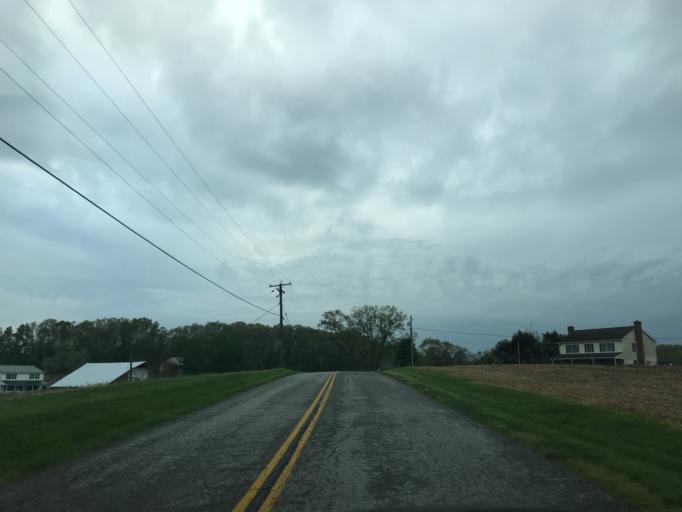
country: US
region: Maryland
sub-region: Harford County
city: Jarrettsville
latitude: 39.6678
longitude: -76.4805
